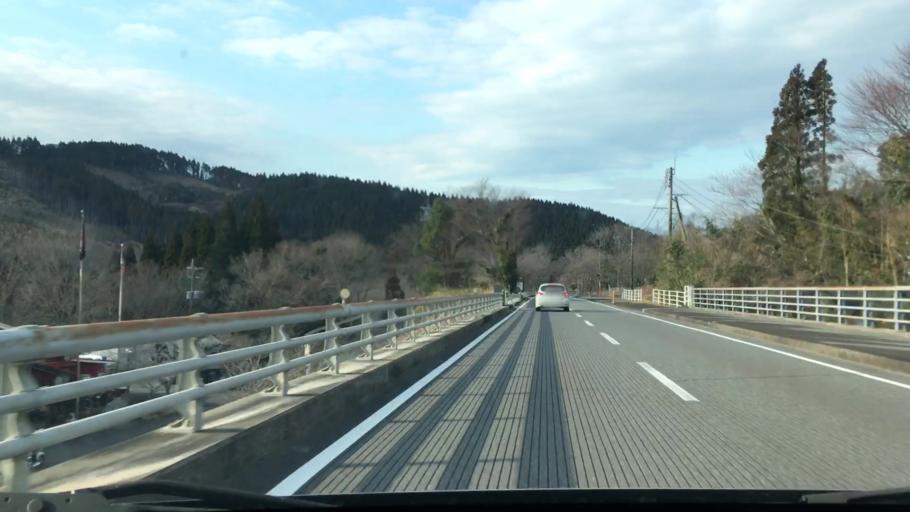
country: JP
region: Miyazaki
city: Miyazaki-shi
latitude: 31.8005
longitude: 131.3029
